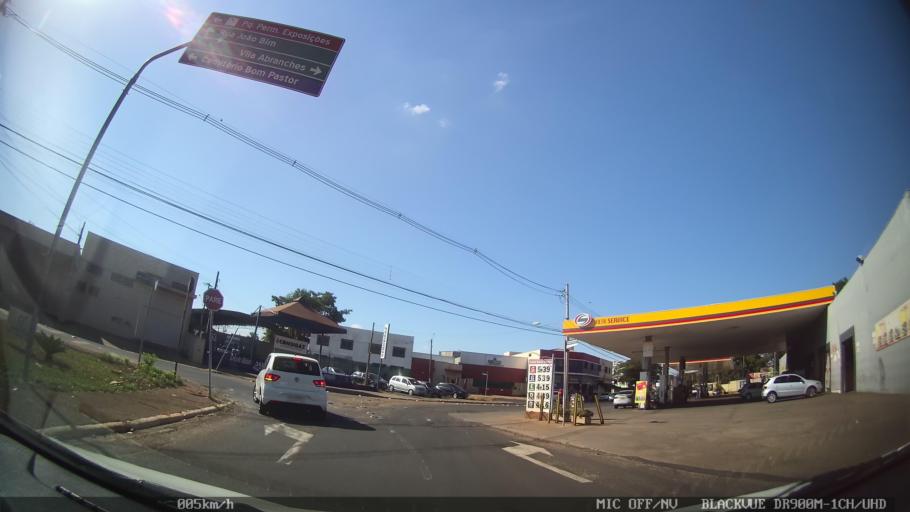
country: BR
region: Sao Paulo
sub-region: Ribeirao Preto
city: Ribeirao Preto
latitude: -21.1843
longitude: -47.7607
